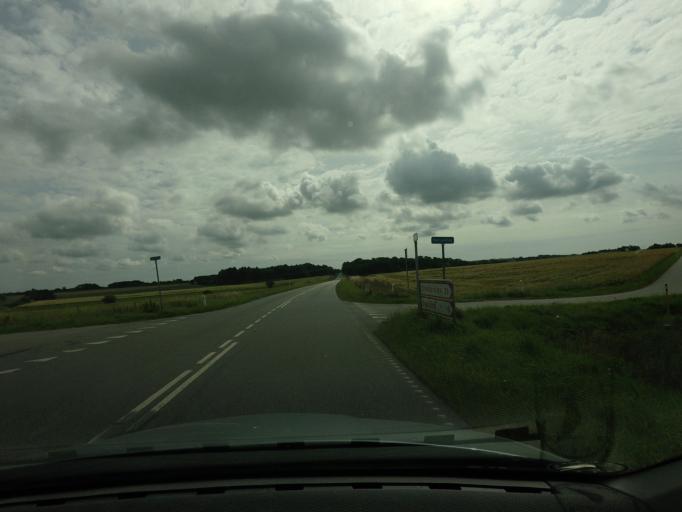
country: DK
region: North Denmark
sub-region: Bronderslev Kommune
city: Dronninglund
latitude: 57.2875
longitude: 10.3131
